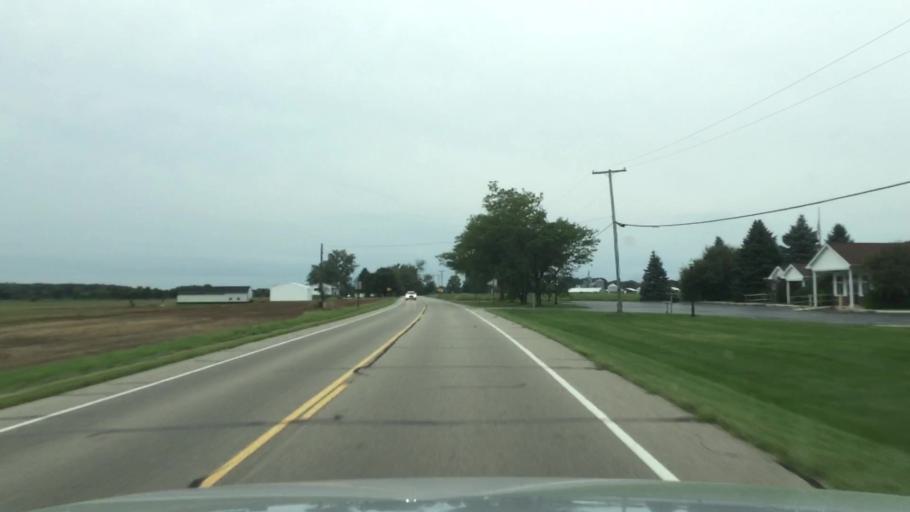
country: US
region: Michigan
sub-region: Washtenaw County
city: Milan
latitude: 42.1195
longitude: -83.7058
